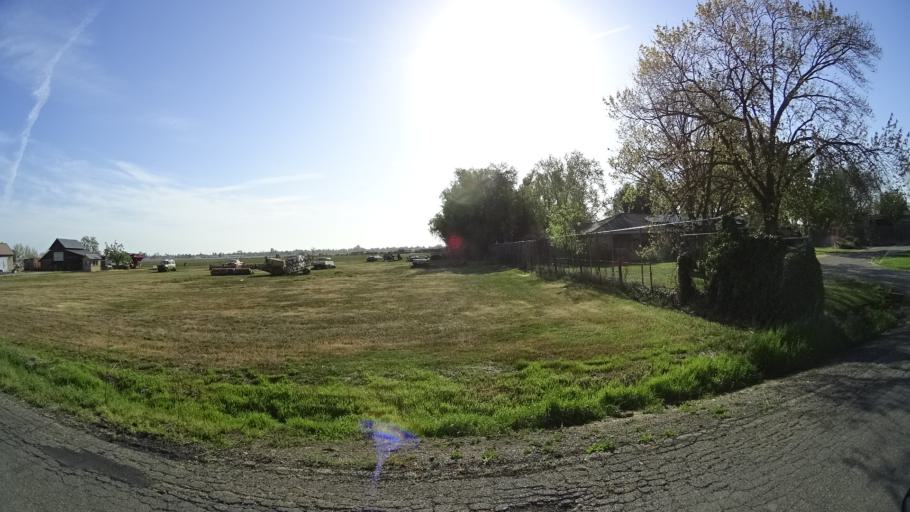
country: US
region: California
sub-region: Glenn County
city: Willows
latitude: 39.5136
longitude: -122.2299
